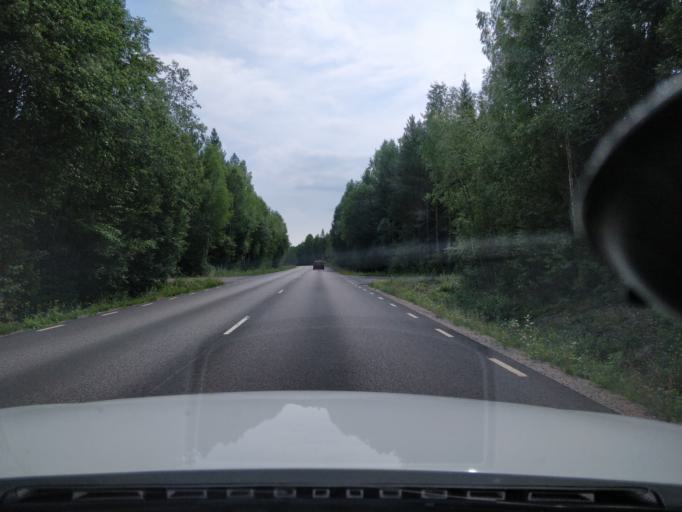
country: SE
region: Dalarna
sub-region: Ludvika Kommun
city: Ludvika
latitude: 60.2925
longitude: 15.2308
